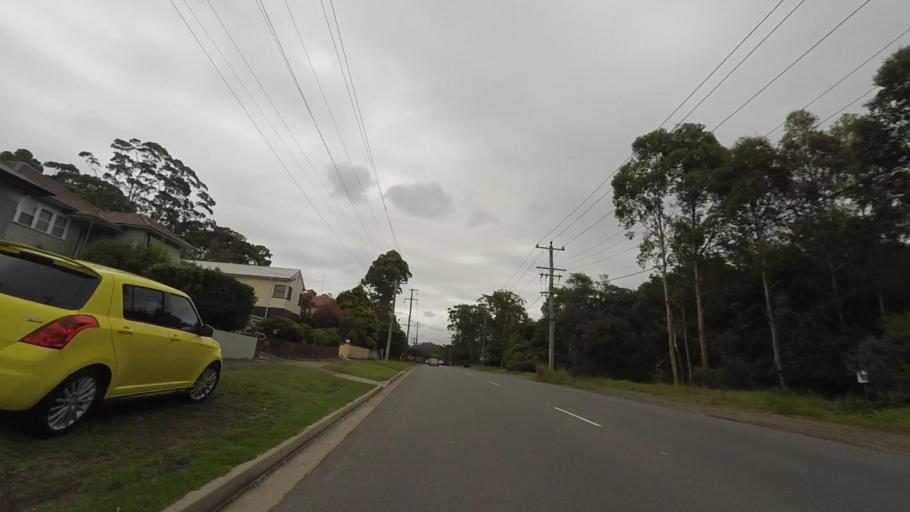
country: AU
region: New South Wales
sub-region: Lake Macquarie Shire
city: Kotara
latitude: -32.9428
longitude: 151.6969
